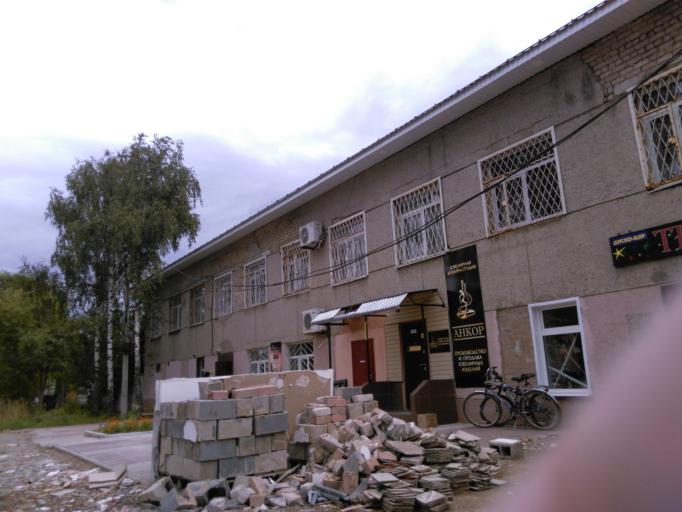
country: RU
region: Ivanovo
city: Privolzhsk
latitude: 57.3792
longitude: 41.2988
